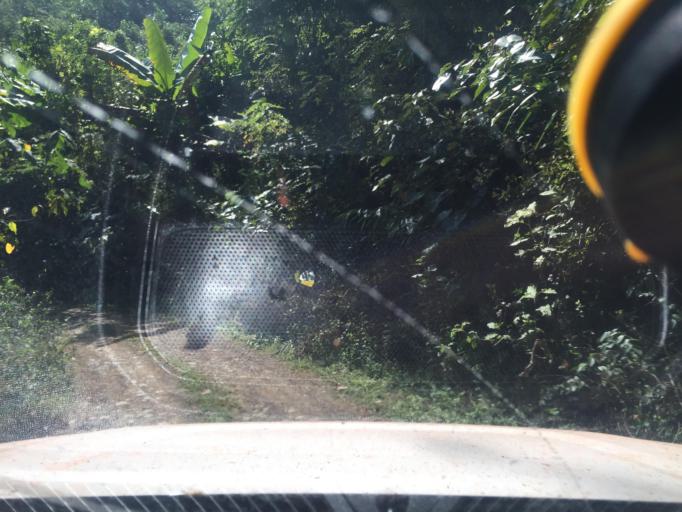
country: LA
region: Phongsali
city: Phongsali
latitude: 21.7043
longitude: 102.3966
